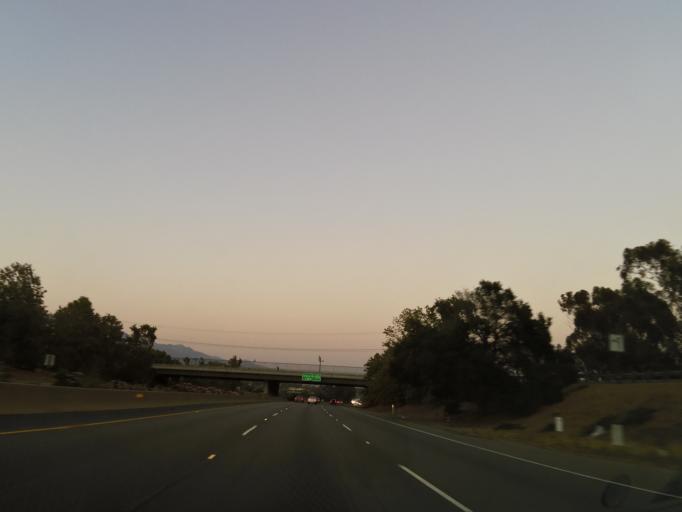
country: US
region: California
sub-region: Santa Barbara County
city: Goleta
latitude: 34.4421
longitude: -119.7911
